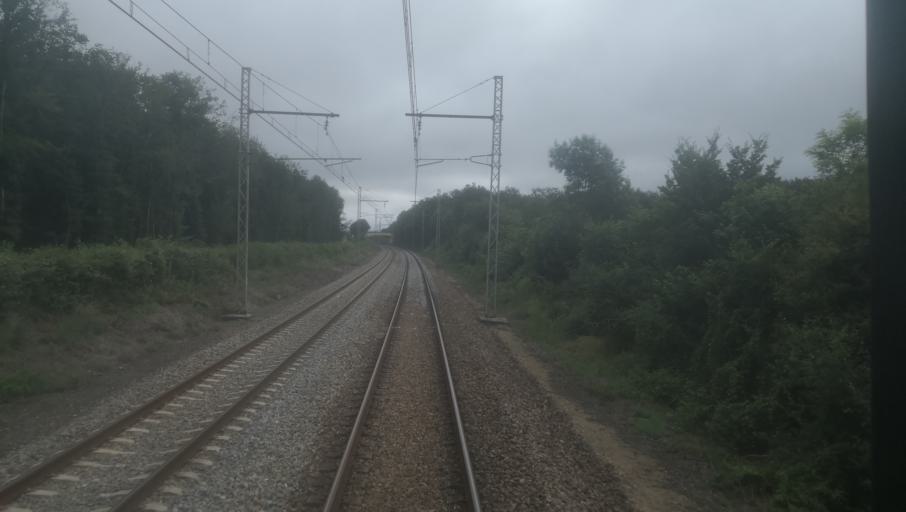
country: FR
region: Centre
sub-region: Departement de l'Indre
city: Saint-Maur
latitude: 46.7728
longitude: 1.6281
